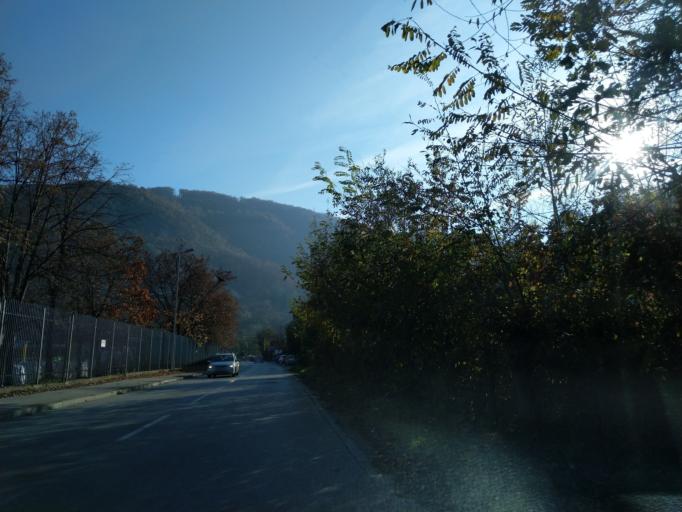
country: RS
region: Central Serbia
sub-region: Zlatiborski Okrug
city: Uzice
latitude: 43.8397
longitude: 19.8853
